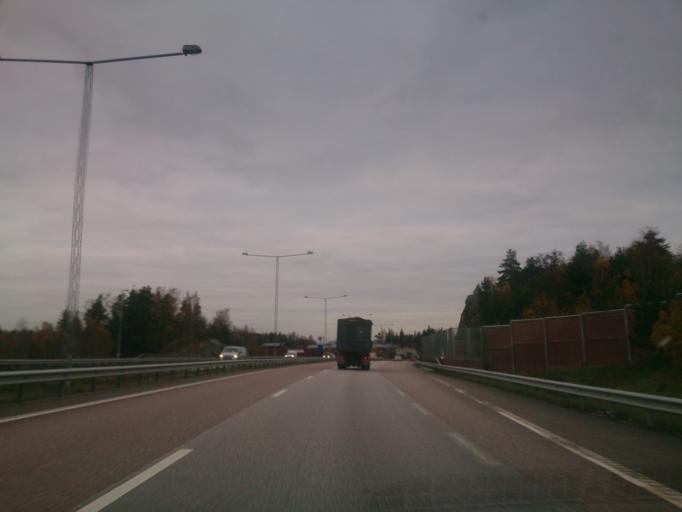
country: SE
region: Stockholm
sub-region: Sodertalje Kommun
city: Pershagen
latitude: 59.1550
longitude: 17.6448
